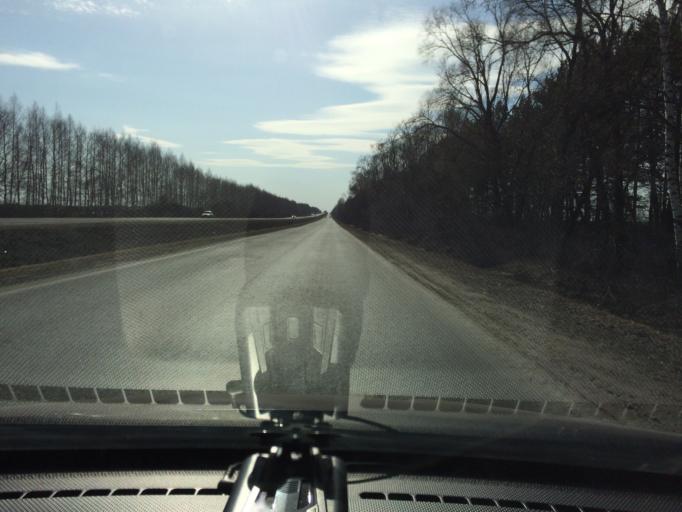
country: RU
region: Mariy-El
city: Yoshkar-Ola
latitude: 56.7348
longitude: 48.1621
